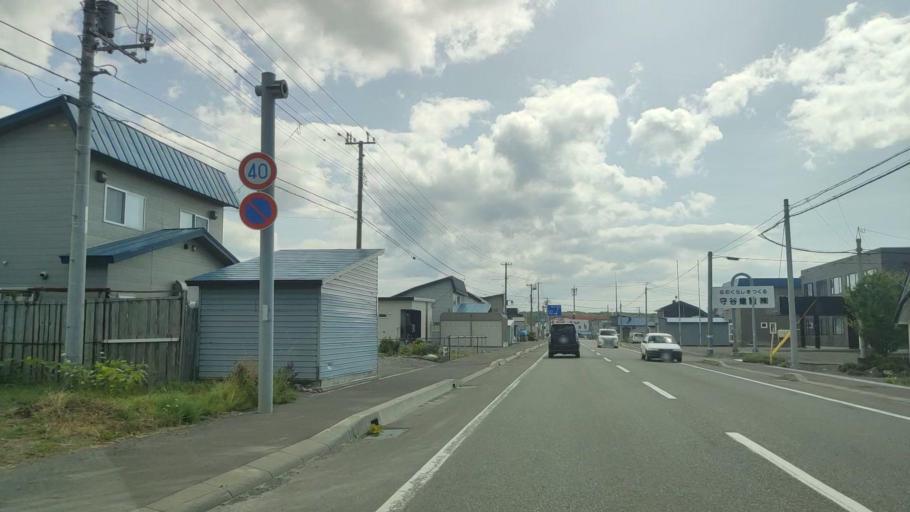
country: JP
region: Hokkaido
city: Makubetsu
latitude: 44.7279
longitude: 141.7990
